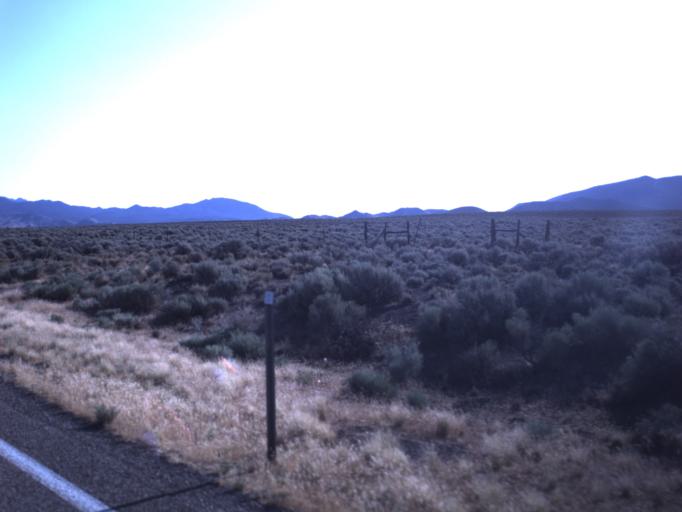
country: US
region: Utah
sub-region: Beaver County
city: Milford
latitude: 38.1629
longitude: -112.9555
